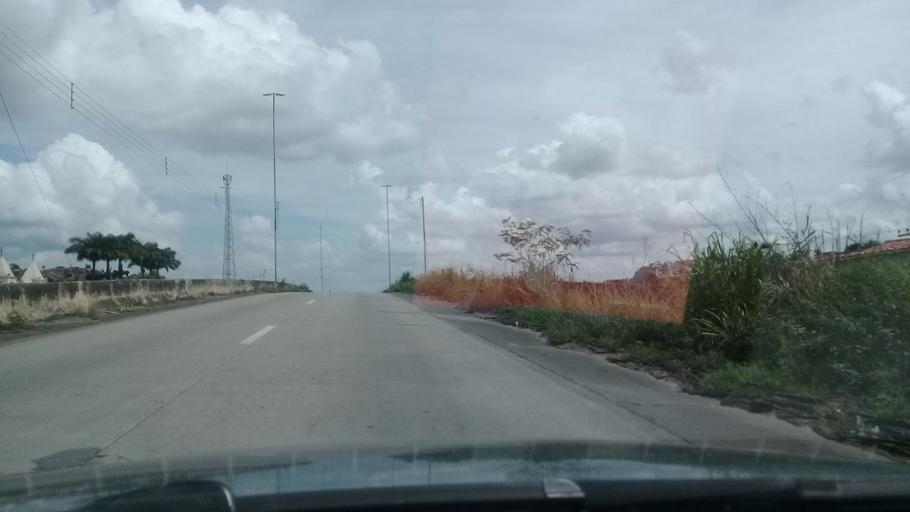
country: BR
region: Pernambuco
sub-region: Moreno
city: Moreno
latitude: -8.1081
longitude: -35.1880
